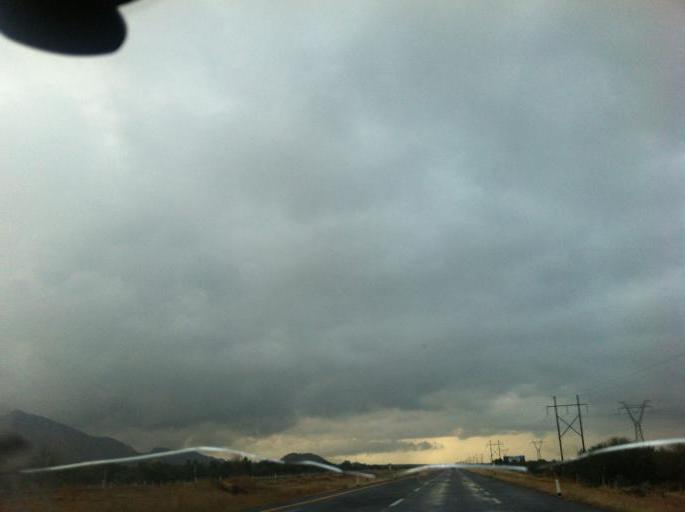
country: MX
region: Sonora
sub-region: Hermosillo
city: Estacion Zamora
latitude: 29.2246
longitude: -110.9311
